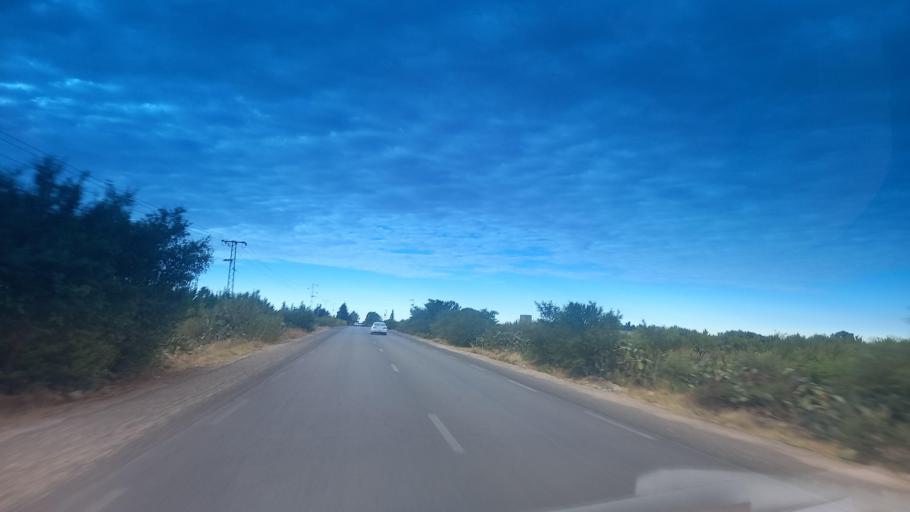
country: TN
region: Al Qasrayn
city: Sbiba
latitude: 35.3050
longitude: 9.0872
